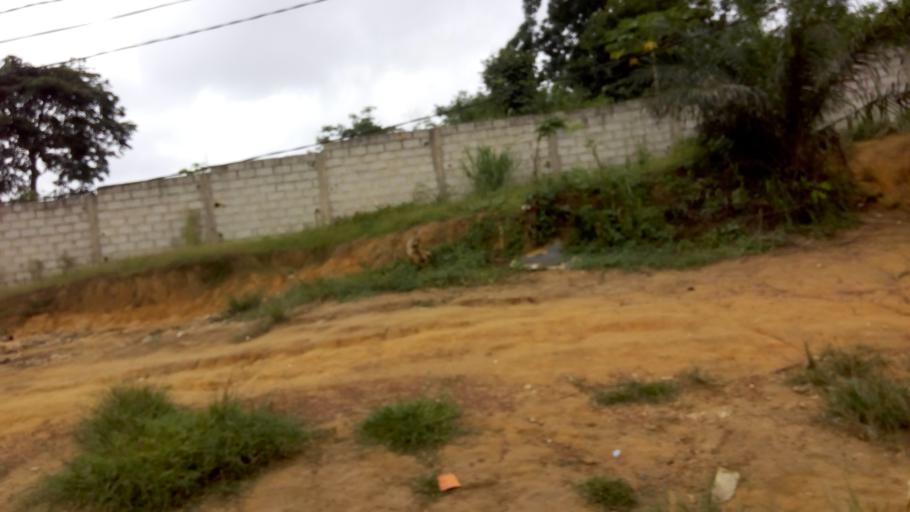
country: CI
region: Lagunes
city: Abidjan
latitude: 5.3372
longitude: -4.1196
